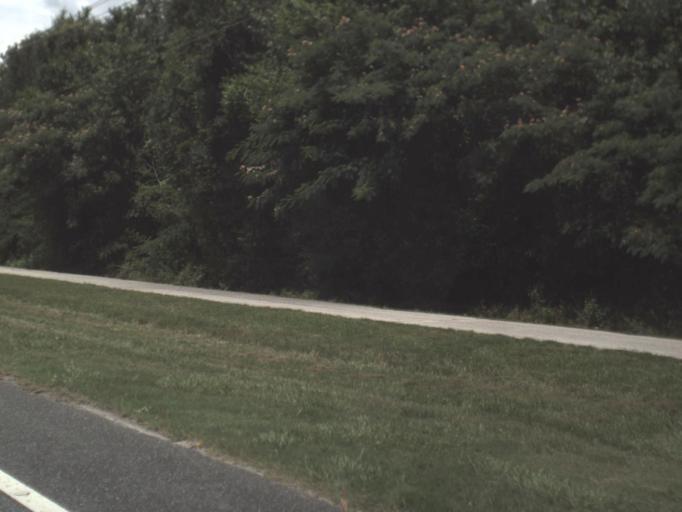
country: US
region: Florida
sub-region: Lafayette County
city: Mayo
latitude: 29.9956
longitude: -82.9357
